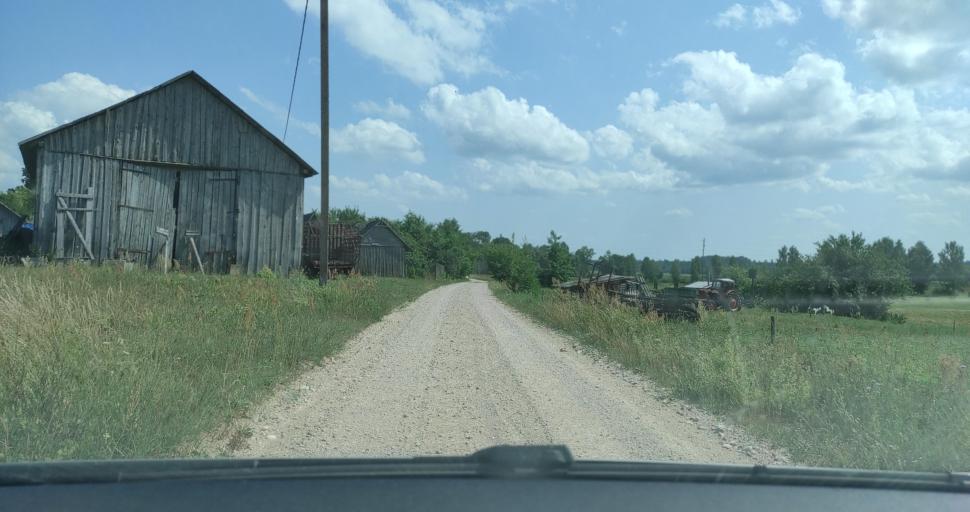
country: LV
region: Kuldigas Rajons
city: Kuldiga
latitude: 57.0653
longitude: 22.2416
